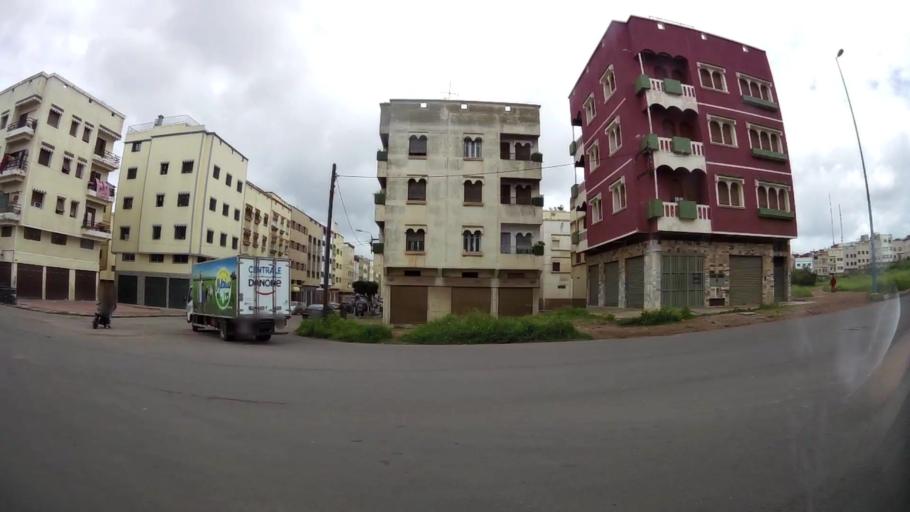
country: MA
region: Grand Casablanca
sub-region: Casablanca
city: Casablanca
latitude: 33.5354
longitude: -7.5908
